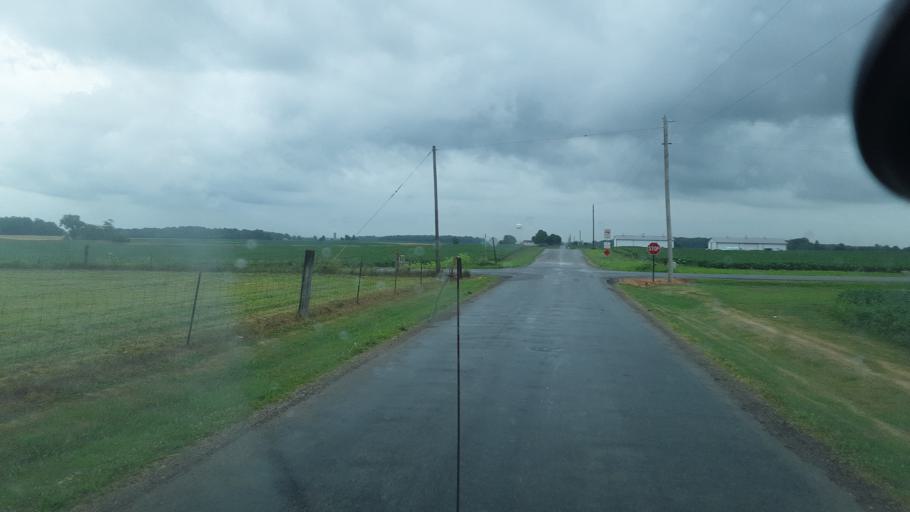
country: US
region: Ohio
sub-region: Williams County
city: Edgerton
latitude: 41.5708
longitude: -84.7891
